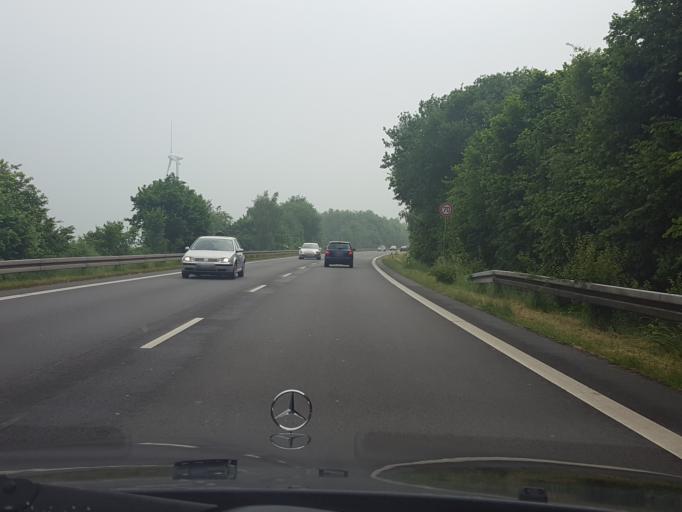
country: DE
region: North Rhine-Westphalia
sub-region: Regierungsbezirk Munster
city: Recklinghausen
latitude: 51.6344
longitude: 7.2078
